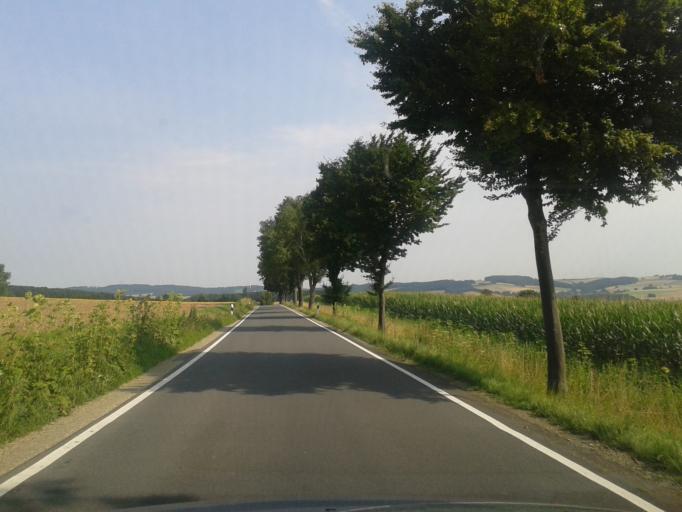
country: DE
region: North Rhine-Westphalia
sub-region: Regierungsbezirk Detmold
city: Blomberg
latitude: 51.9899
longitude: 9.0554
